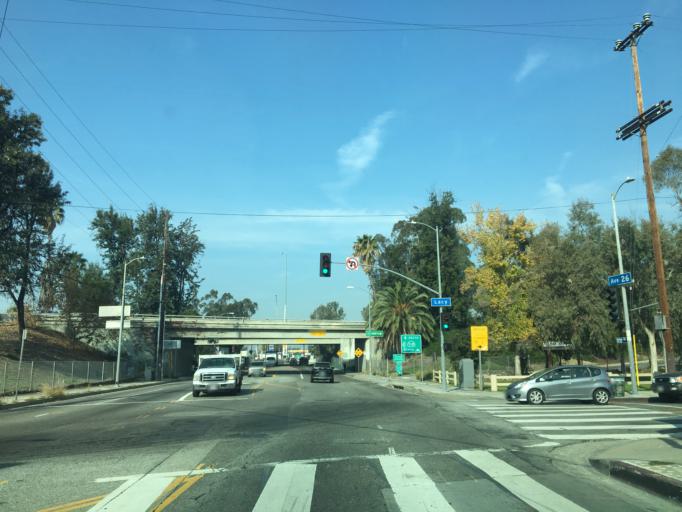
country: US
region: California
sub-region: Los Angeles County
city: Los Angeles
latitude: 34.0818
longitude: -118.2203
